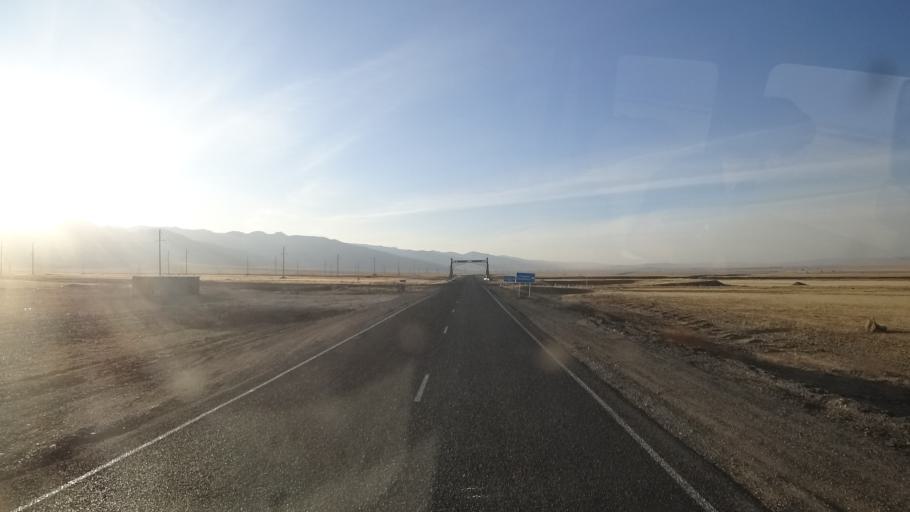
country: KZ
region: Zhambyl
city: Karatau
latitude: 42.9529
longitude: 70.6607
